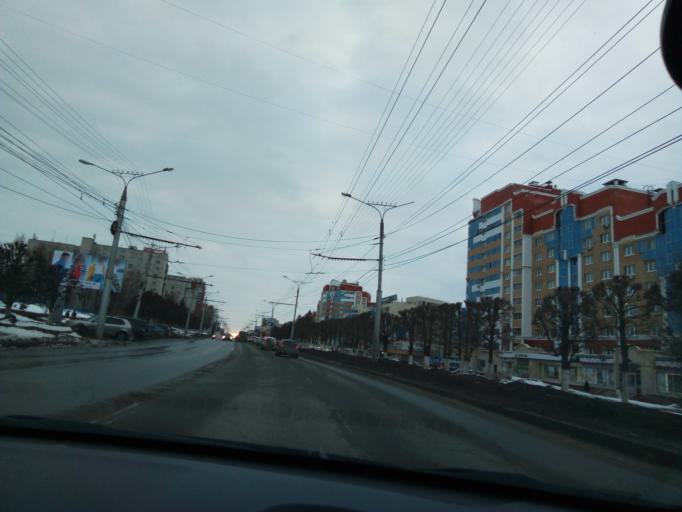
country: RU
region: Chuvashia
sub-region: Cheboksarskiy Rayon
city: Cheboksary
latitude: 56.1487
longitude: 47.1992
